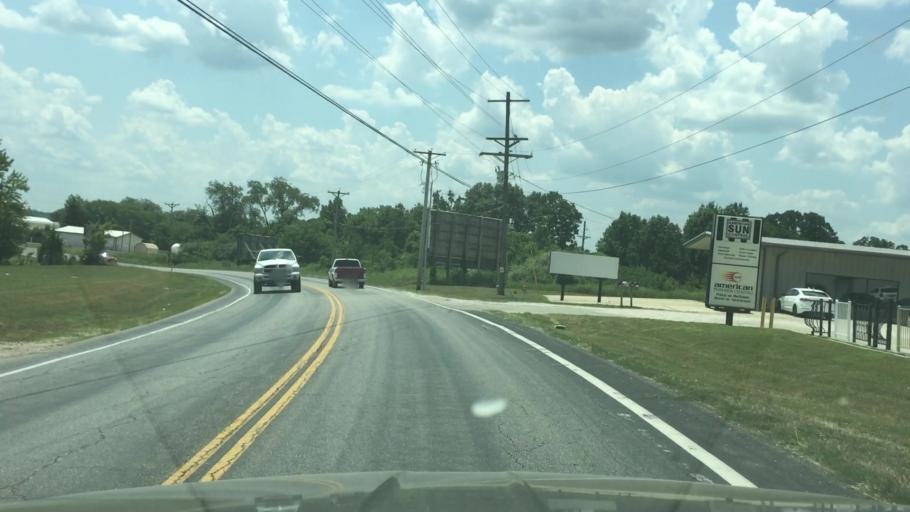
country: US
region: Missouri
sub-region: Camden County
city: Osage Beach
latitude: 38.1412
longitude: -92.5913
